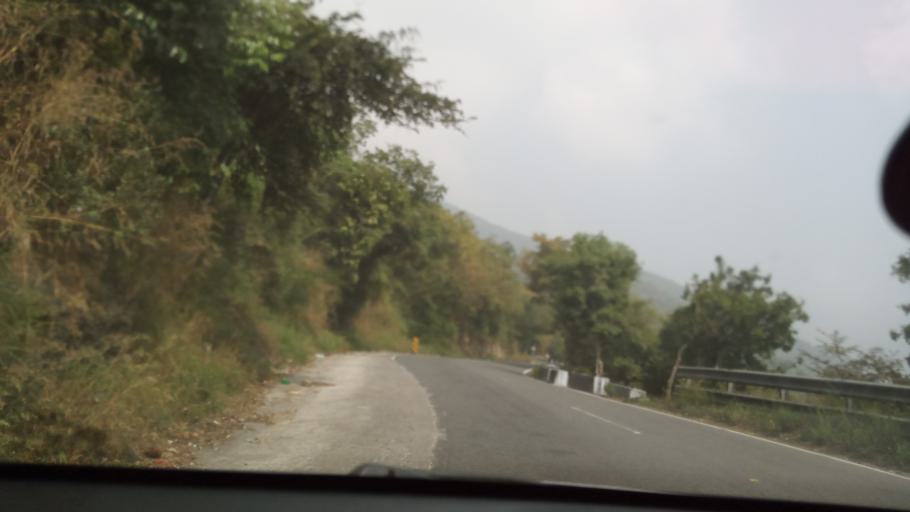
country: IN
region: Tamil Nadu
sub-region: Erode
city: Sathyamangalam
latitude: 11.5931
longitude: 77.1271
